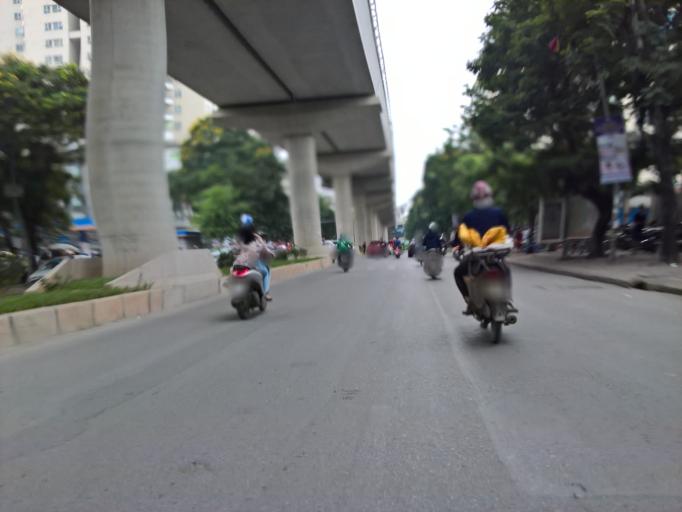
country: VN
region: Ha Noi
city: Cau Giay
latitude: 21.0367
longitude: 105.7862
